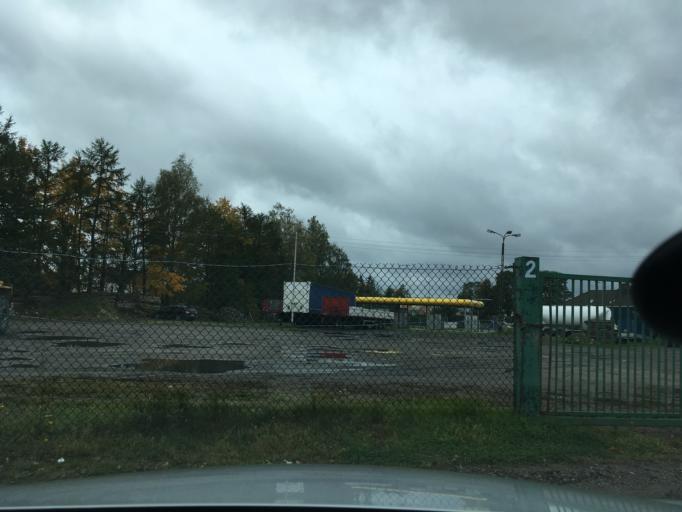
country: PL
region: Pomeranian Voivodeship
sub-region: Powiat koscierski
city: Koscierzyna
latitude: 54.1190
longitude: 17.9951
